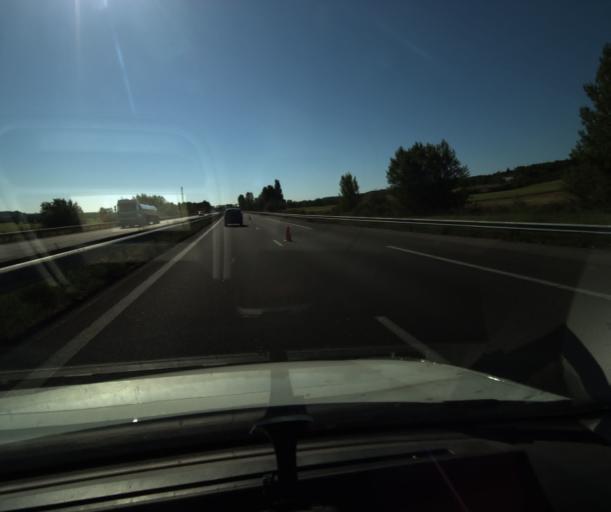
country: FR
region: Languedoc-Roussillon
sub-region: Departement de l'Aude
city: Villeneuve-la-Comptal
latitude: 43.3220
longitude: 1.8644
